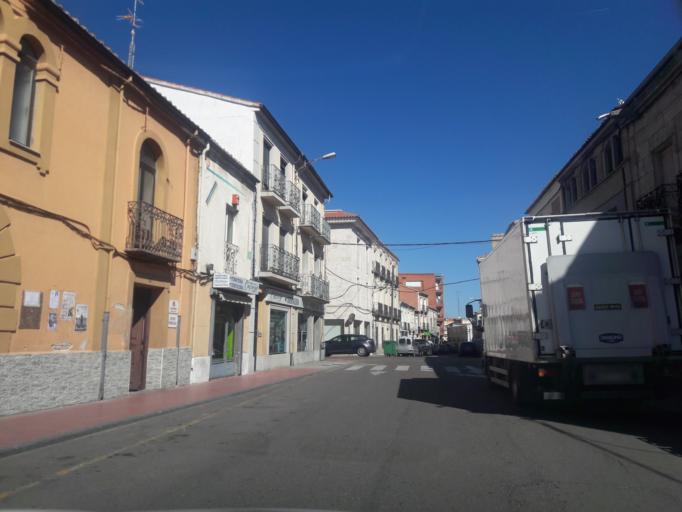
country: ES
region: Castille and Leon
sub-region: Provincia de Salamanca
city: Penaranda de Bracamonte
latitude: 40.9003
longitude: -5.2012
